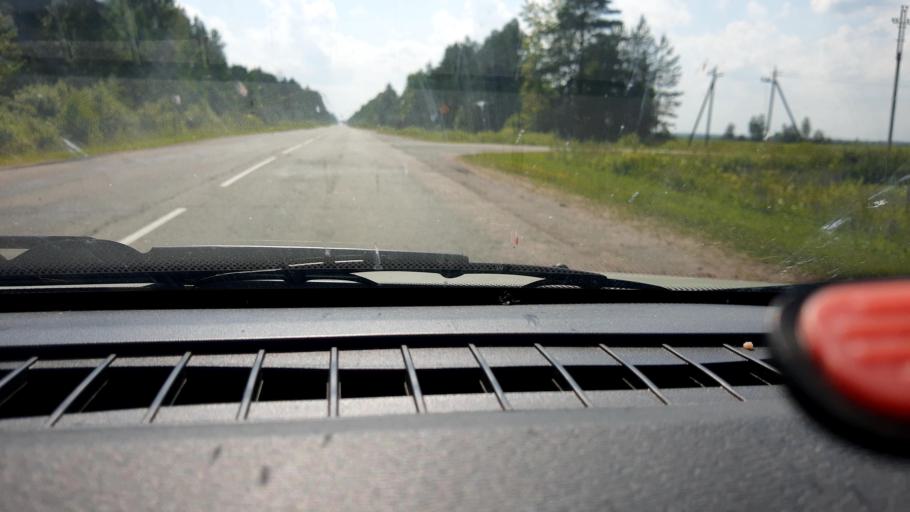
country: RU
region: Nizjnij Novgorod
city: Tonkino
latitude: 57.3669
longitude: 46.3440
